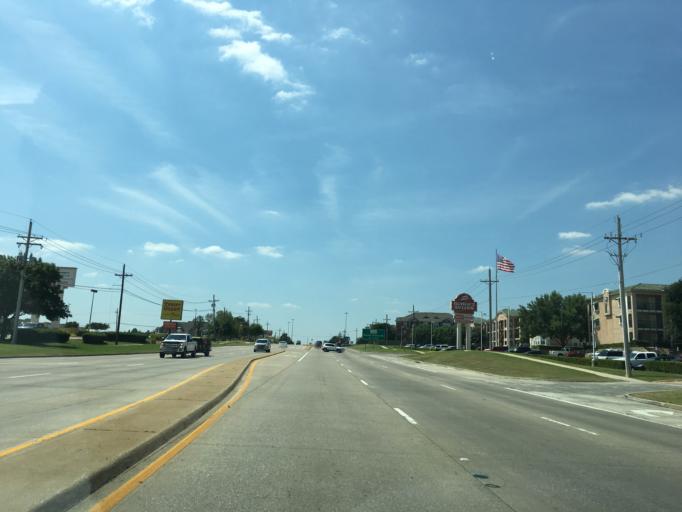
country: US
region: Texas
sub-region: Denton County
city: Lewisville
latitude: 33.0114
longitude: -96.9931
